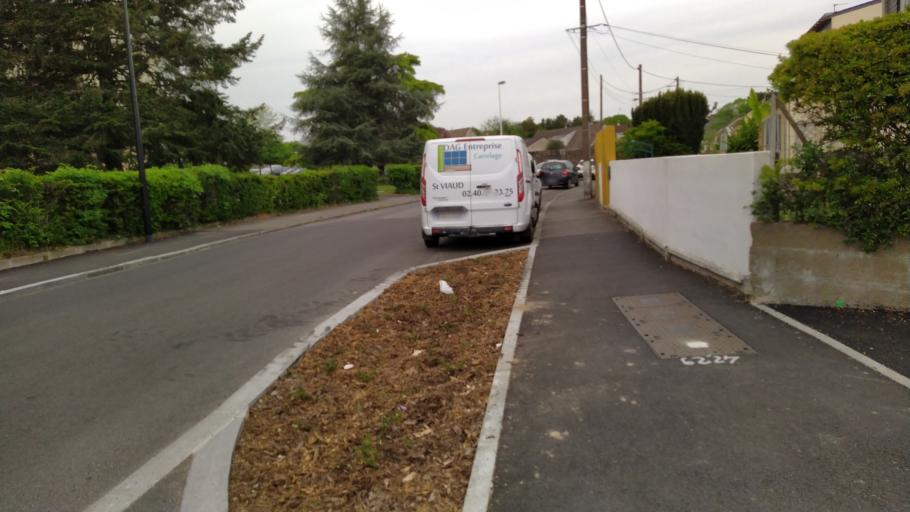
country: FR
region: Pays de la Loire
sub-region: Departement de la Loire-Atlantique
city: Saint-Herblain
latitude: 47.2232
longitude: -1.6070
